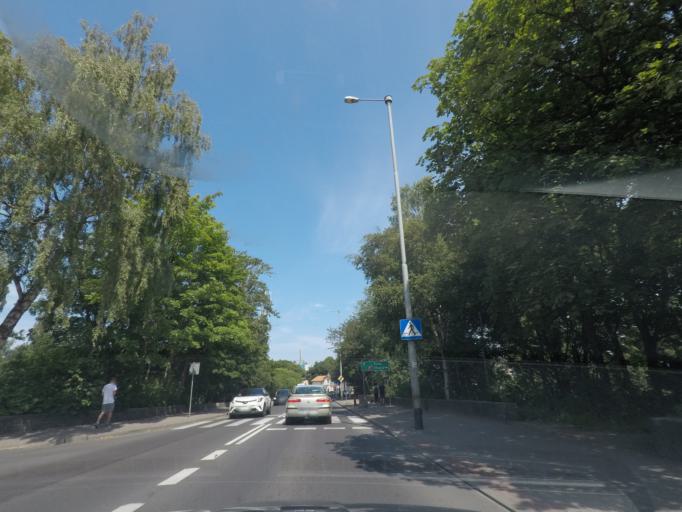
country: PL
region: Pomeranian Voivodeship
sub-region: Powiat slupski
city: Ustka
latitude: 54.5796
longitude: 16.8608
